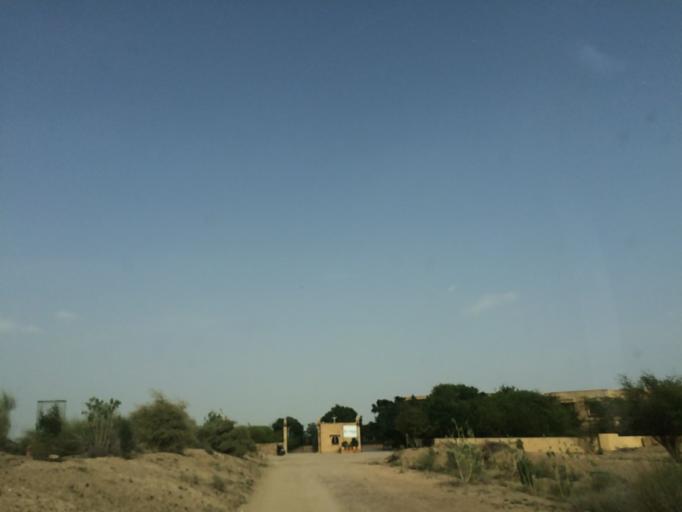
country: IN
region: Rajasthan
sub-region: Jaisalmer
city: Jaisalmer
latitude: 26.8662
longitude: 70.8694
